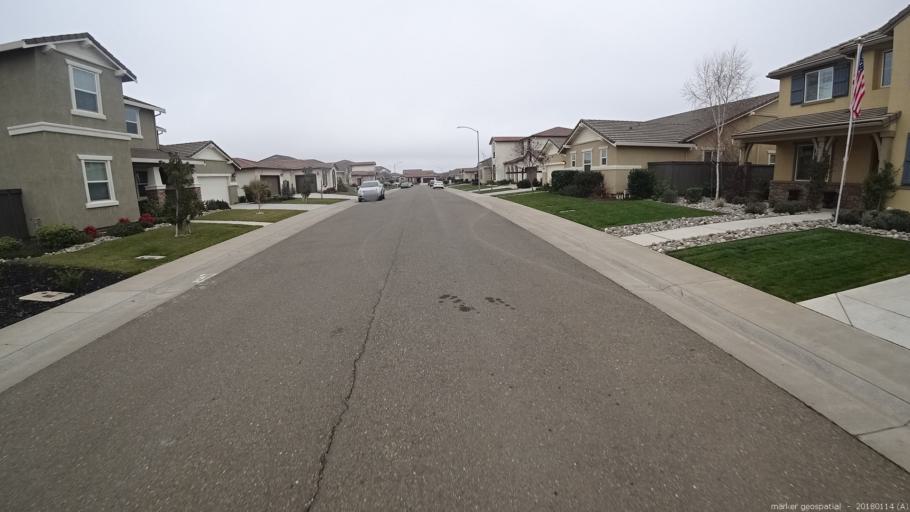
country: US
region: California
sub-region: Sacramento County
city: Rancho Cordova
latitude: 38.5315
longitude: -121.2287
